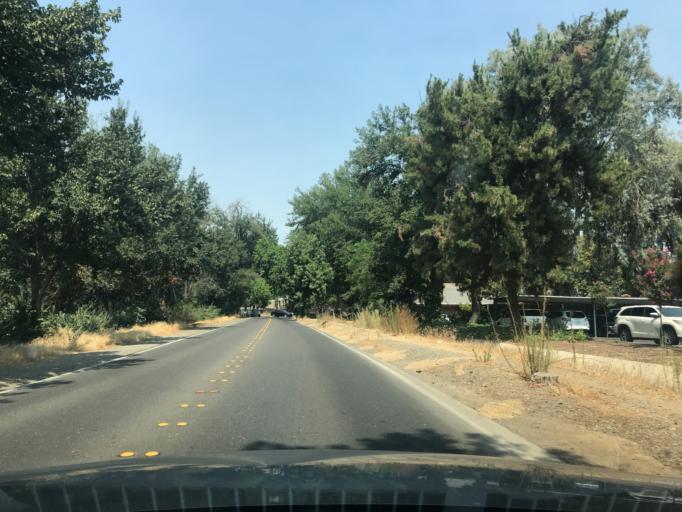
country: US
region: California
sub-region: Merced County
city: Merced
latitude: 37.3110
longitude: -120.4709
